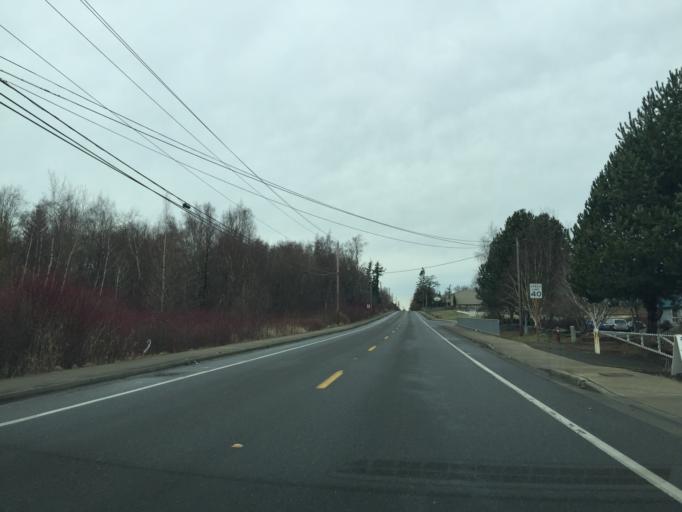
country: US
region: Washington
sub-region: Whatcom County
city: Marietta-Alderwood
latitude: 48.7709
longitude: -122.5243
